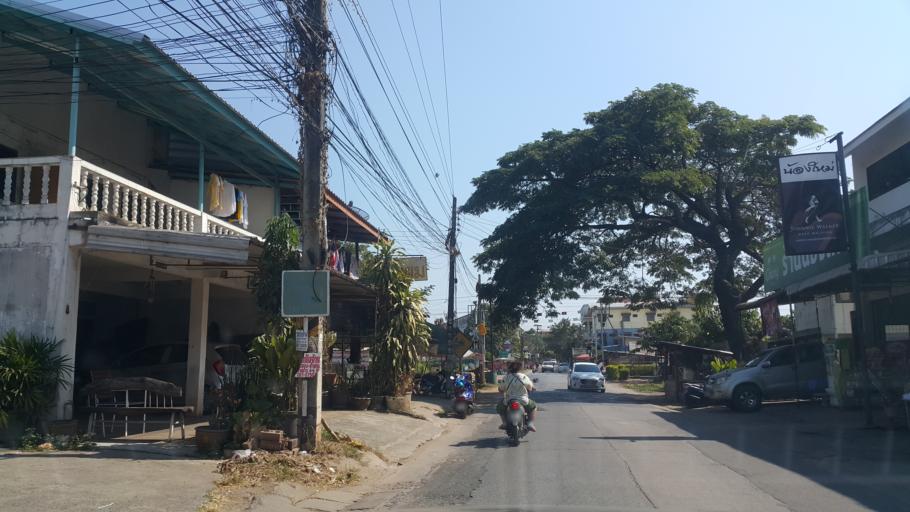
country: TH
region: Changwat Udon Thani
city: Udon Thani
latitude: 17.3920
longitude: 102.8048
